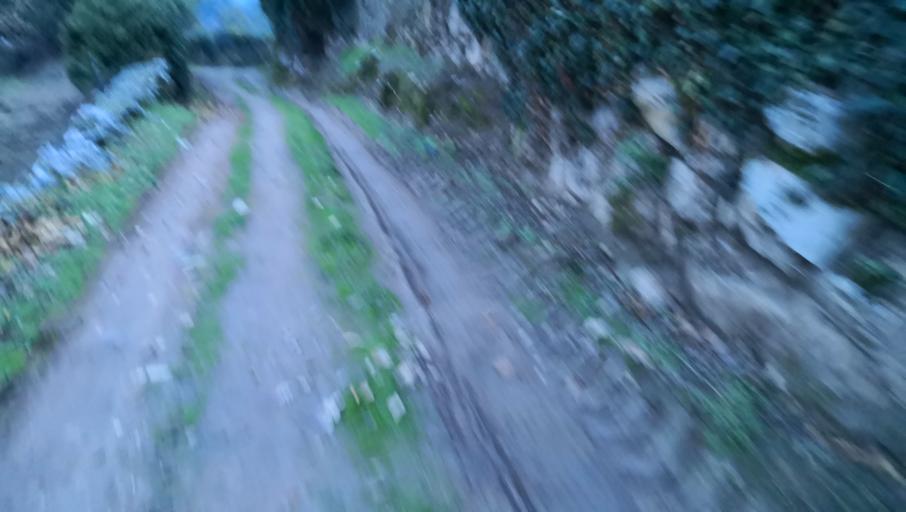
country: PT
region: Vila Real
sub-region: Vila Real
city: Vila Real
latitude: 41.3071
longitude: -7.7179
